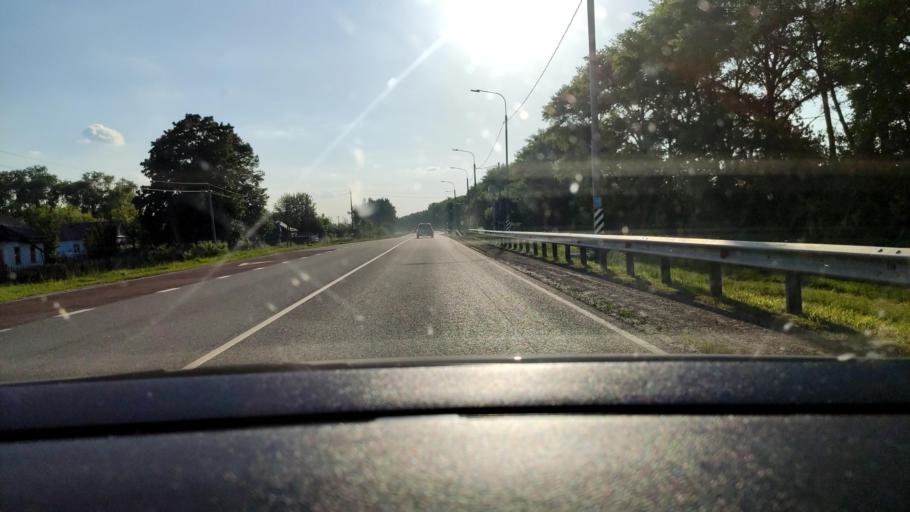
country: RU
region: Voronezj
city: Kashirskoye
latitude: 51.4586
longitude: 39.8028
